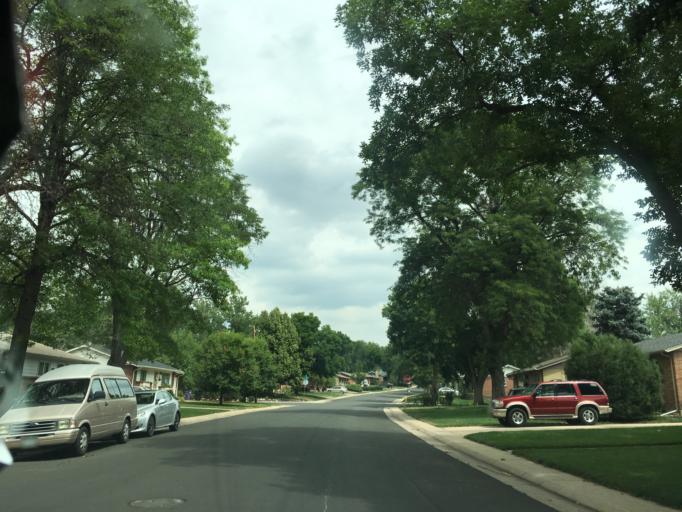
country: US
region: Colorado
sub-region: Arapahoe County
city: Sheridan
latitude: 39.6593
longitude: -105.0479
